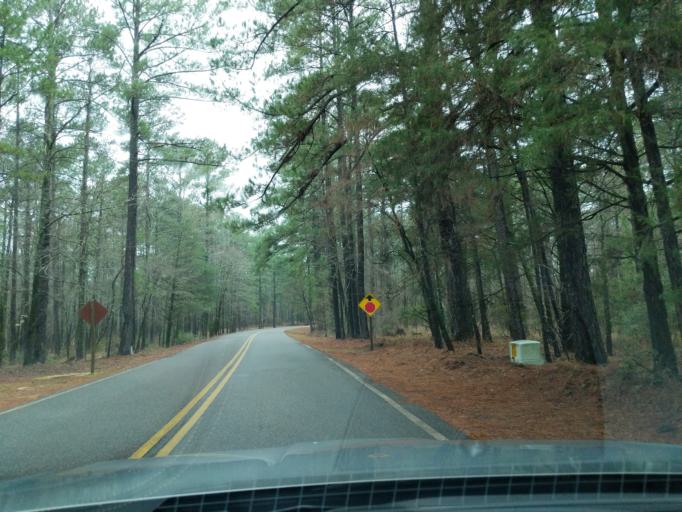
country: US
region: Georgia
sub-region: Columbia County
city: Appling
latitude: 33.6477
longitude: -82.3855
